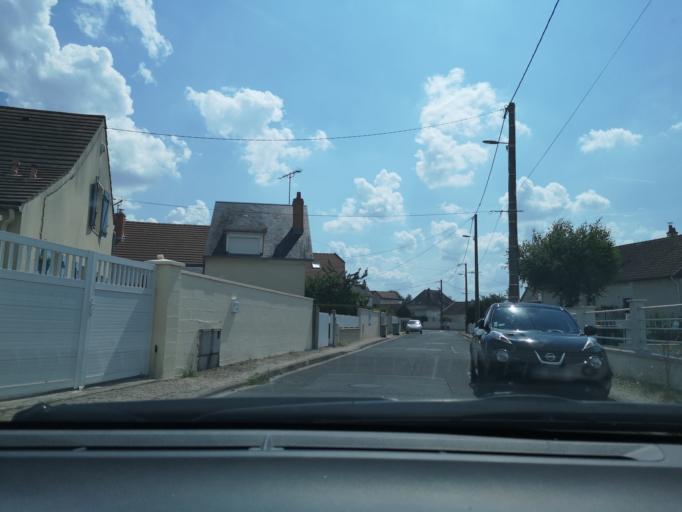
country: FR
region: Centre
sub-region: Departement du Loiret
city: Fleury-les-Aubrais
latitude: 47.9350
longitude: 1.9196
